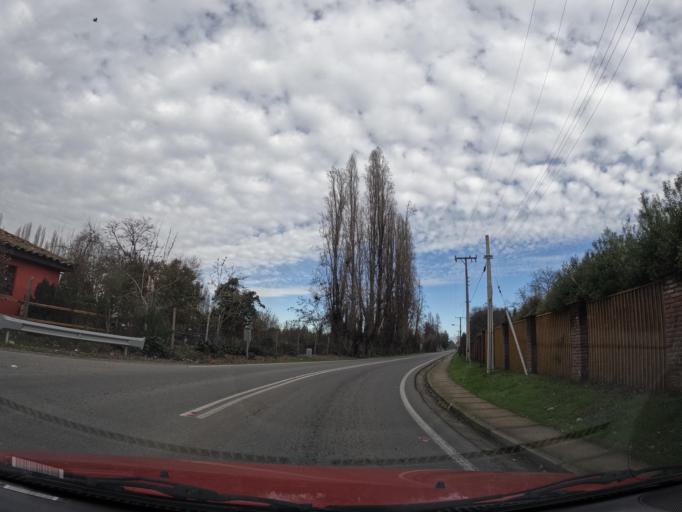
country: CL
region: Maule
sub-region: Provincia de Linares
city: Linares
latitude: -35.8761
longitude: -71.5409
